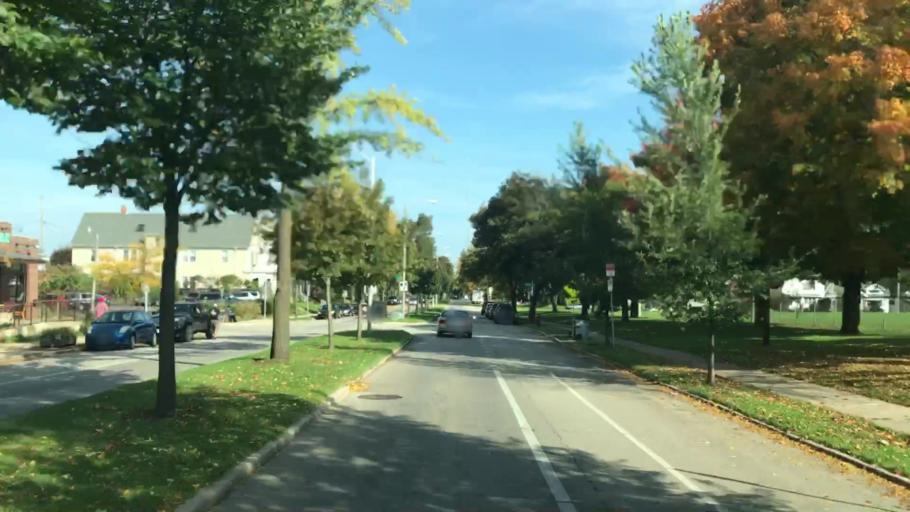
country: US
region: Wisconsin
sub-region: Milwaukee County
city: Shorewood
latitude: 43.0724
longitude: -87.8977
